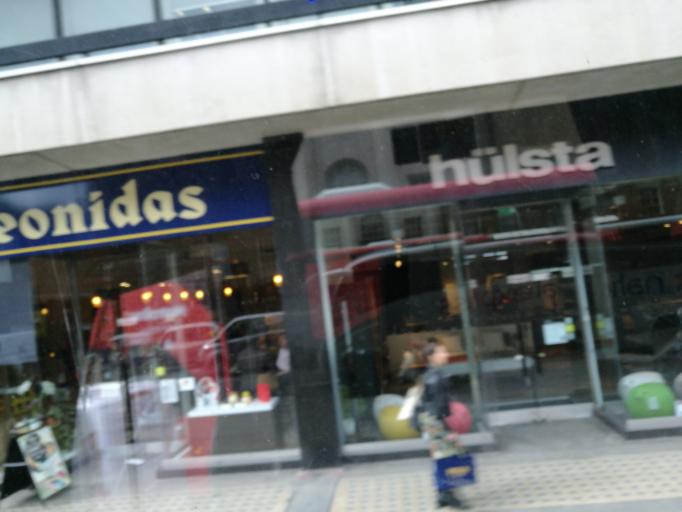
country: GB
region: England
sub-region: Greater London
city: Camden Town
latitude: 51.5177
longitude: -0.1555
